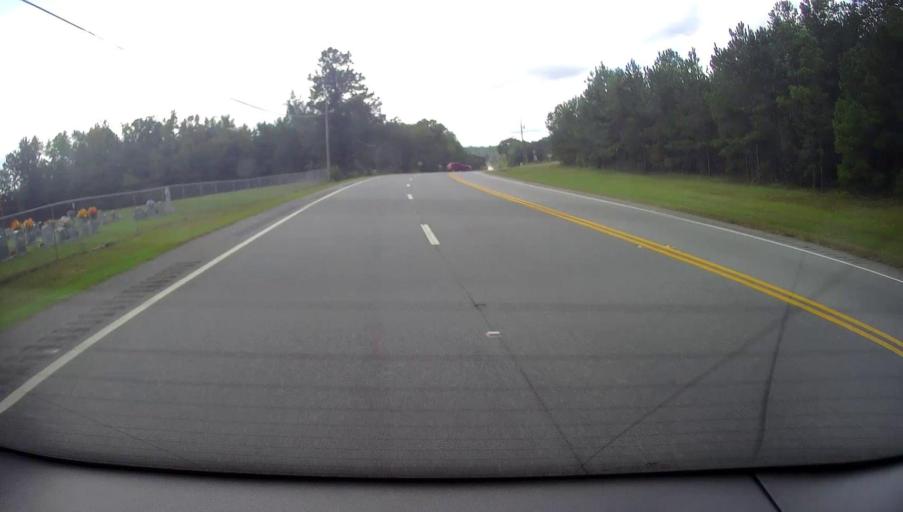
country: US
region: Georgia
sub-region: Baldwin County
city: Milledgeville
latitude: 33.0603
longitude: -83.2762
